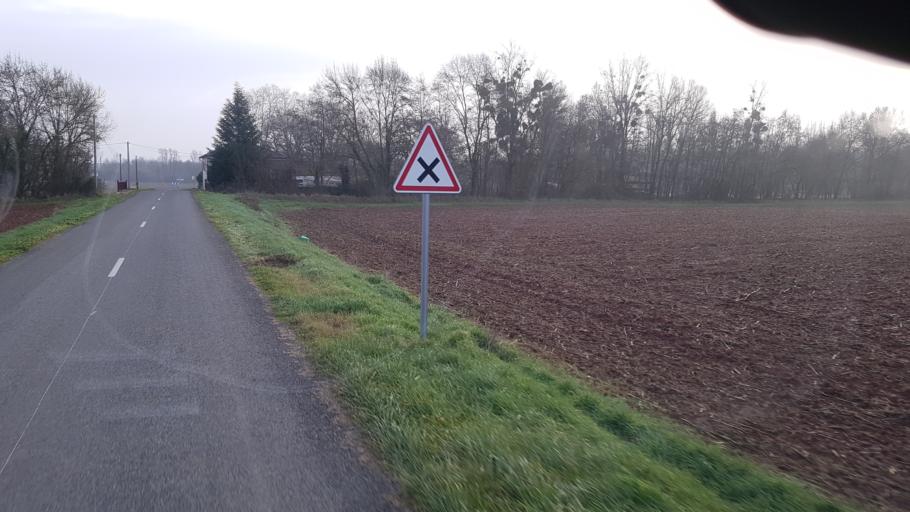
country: FR
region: Midi-Pyrenees
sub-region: Departement du Tarn
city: Cahuzac-sur-Vere
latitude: 43.9823
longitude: 1.8113
